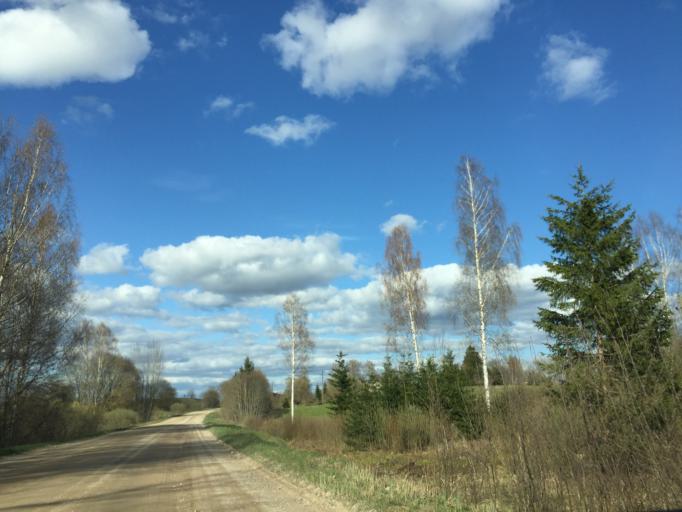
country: LV
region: Rezekne
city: Rezekne
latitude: 56.6368
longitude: 27.3136
